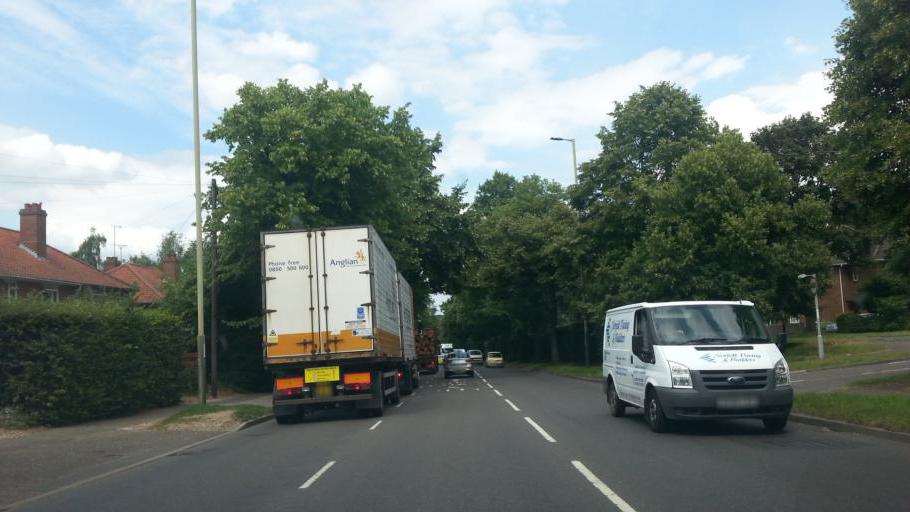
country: GB
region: England
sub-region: Norfolk
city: Cringleford
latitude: 52.6346
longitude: 1.2592
